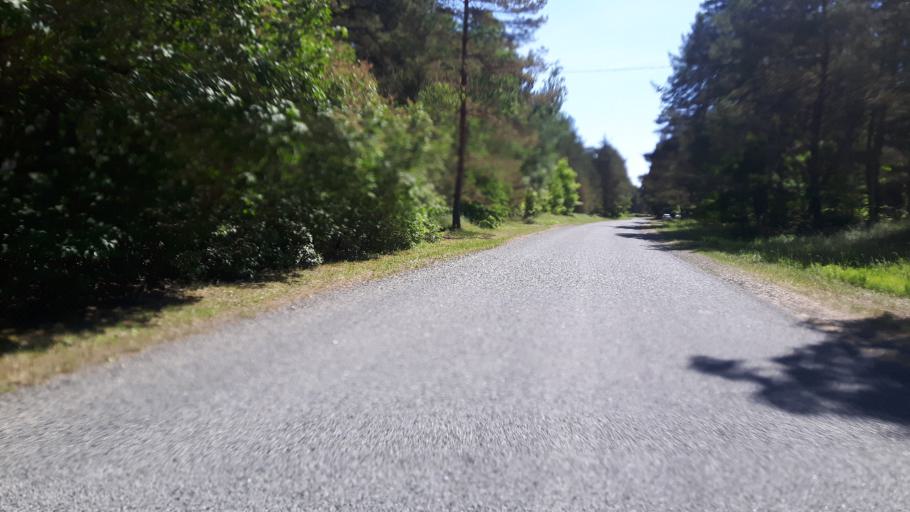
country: LV
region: Salacgrivas
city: Ainazi
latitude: 57.9266
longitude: 24.3912
